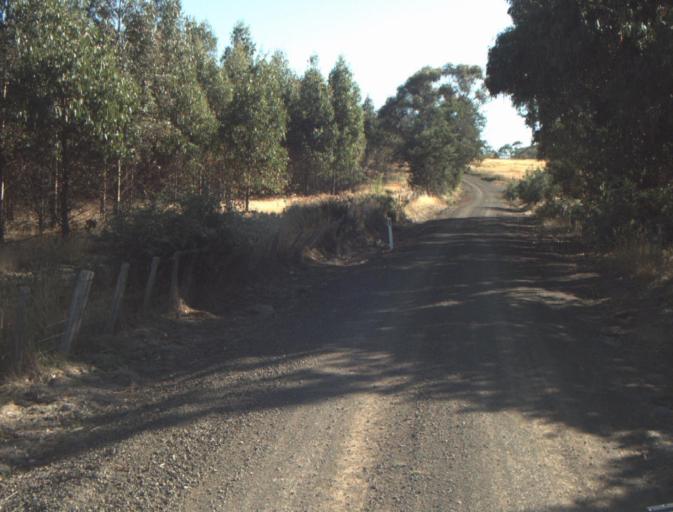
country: AU
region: Tasmania
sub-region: Launceston
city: Newstead
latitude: -41.4122
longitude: 147.2873
